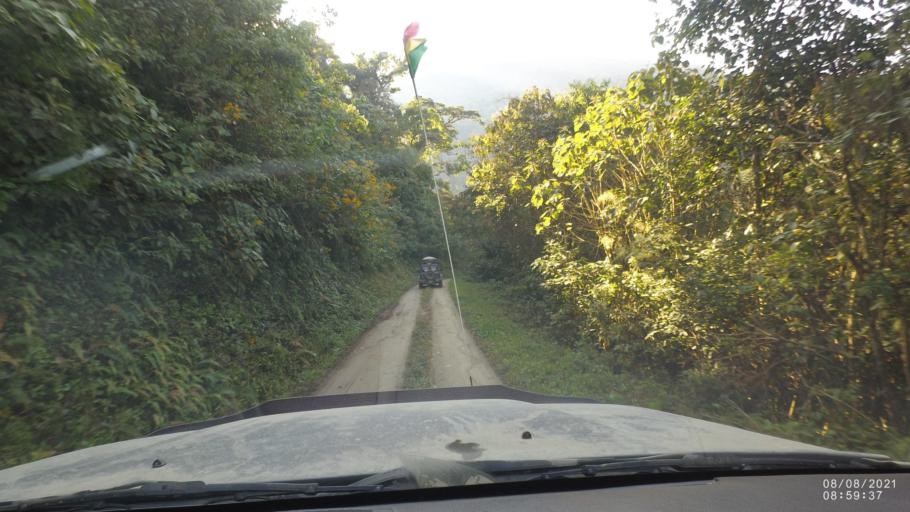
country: BO
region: La Paz
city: Quime
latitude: -16.5504
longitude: -66.7398
